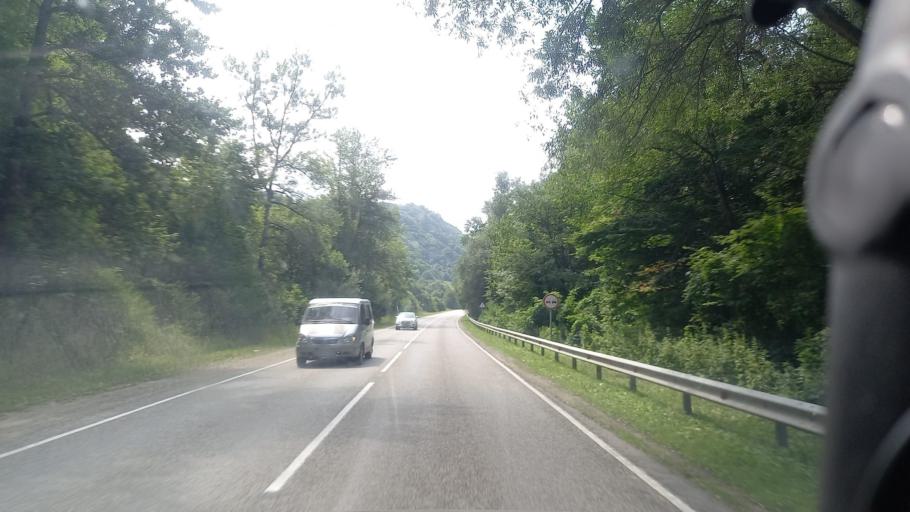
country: RU
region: Krasnodarskiy
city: Psebay
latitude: 44.1589
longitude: 40.8519
